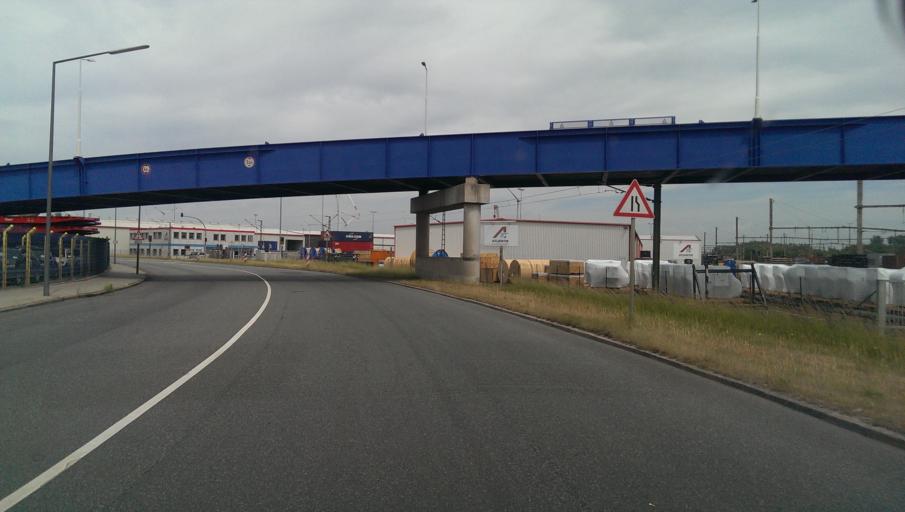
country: DE
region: Bremen
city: Bremerhaven
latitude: 53.5773
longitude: 8.5624
